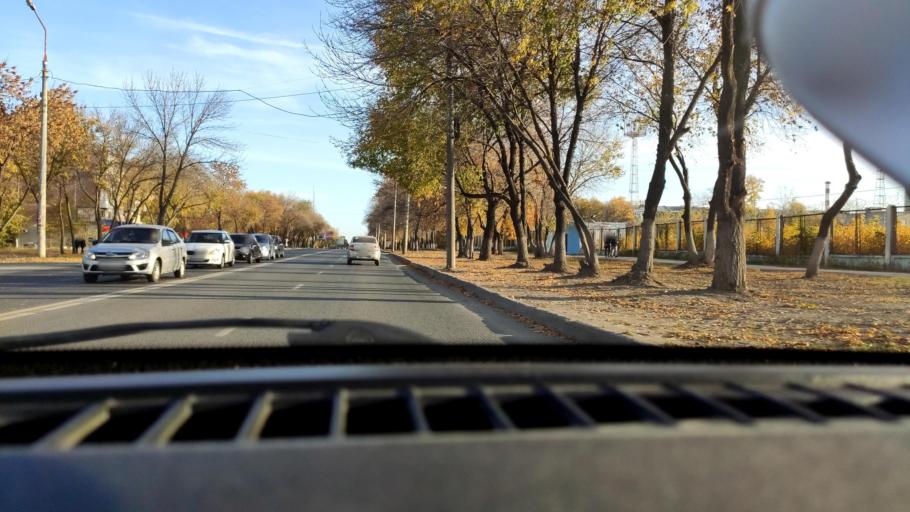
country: RU
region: Samara
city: Samara
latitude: 53.2206
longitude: 50.2040
